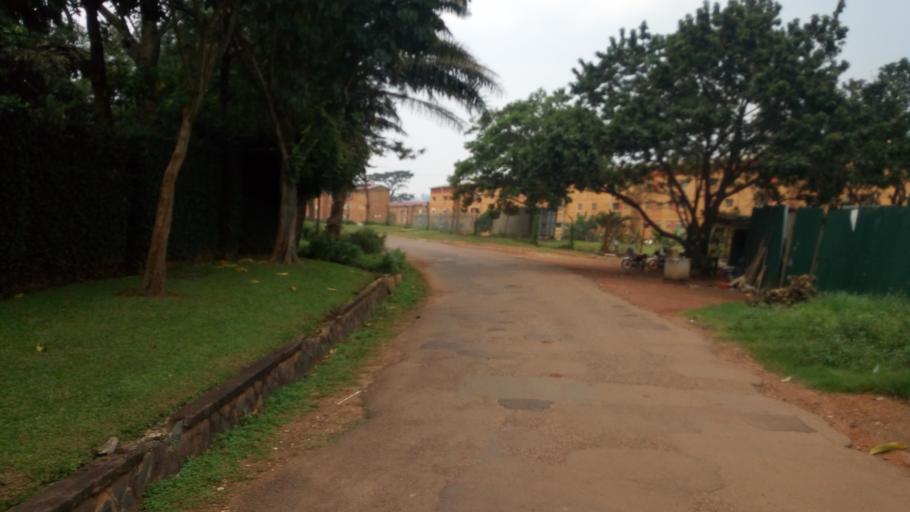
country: UG
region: Central Region
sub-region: Kampala District
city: Kampala
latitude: 0.3086
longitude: 32.6252
